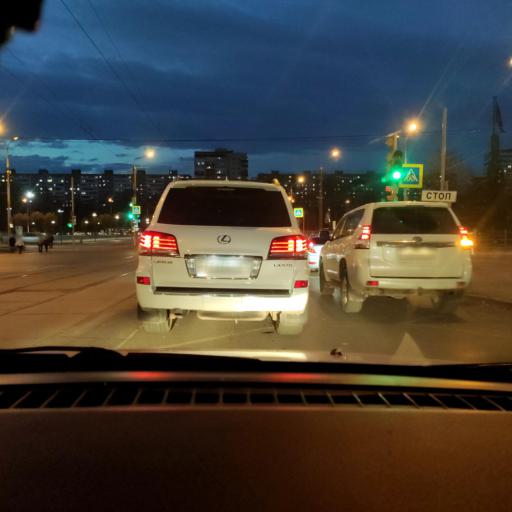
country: RU
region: Perm
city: Perm
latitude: 58.0076
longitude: 56.2202
